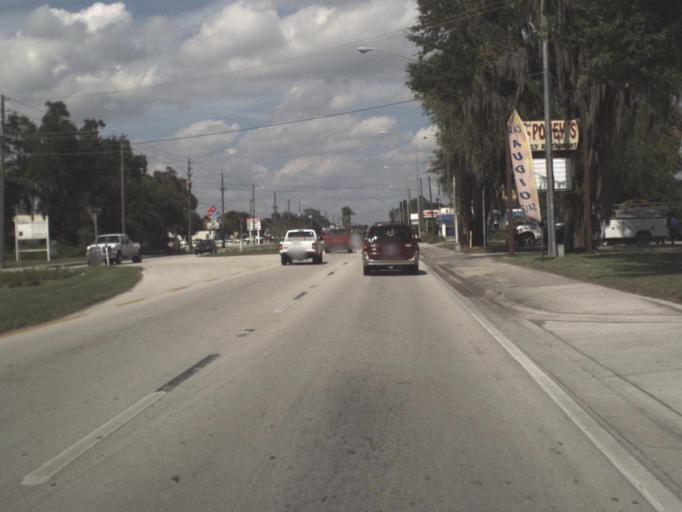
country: US
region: Florida
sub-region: Okeechobee County
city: Okeechobee
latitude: 27.2261
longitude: -80.8298
